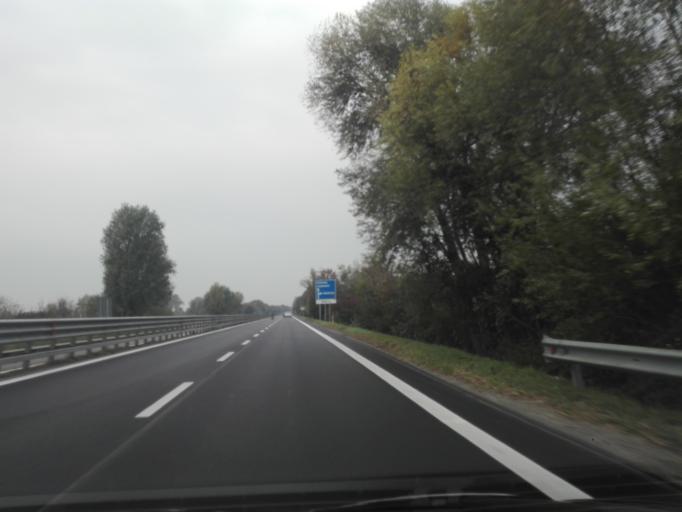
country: IT
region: Veneto
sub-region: Provincia di Verona
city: Villa Bartolomea
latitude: 45.1607
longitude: 11.3109
